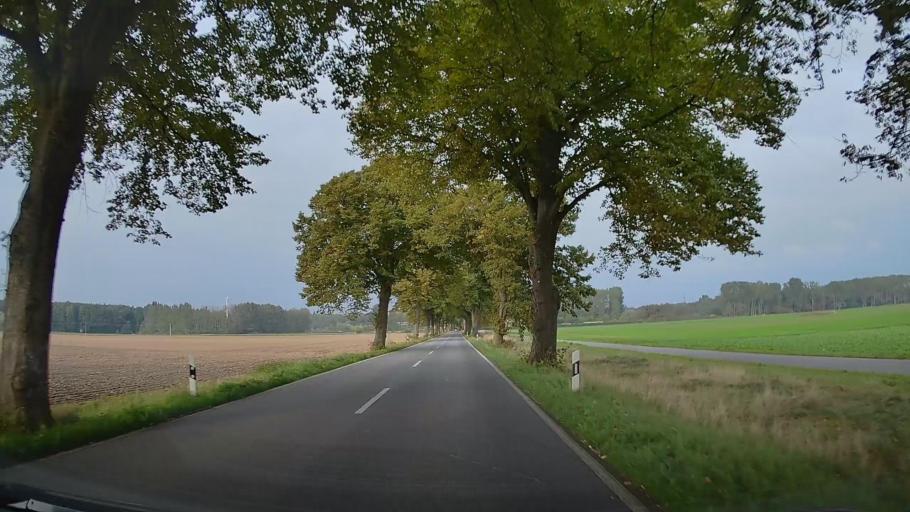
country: DE
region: Mecklenburg-Vorpommern
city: Bad Doberan
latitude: 54.1336
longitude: 11.8350
